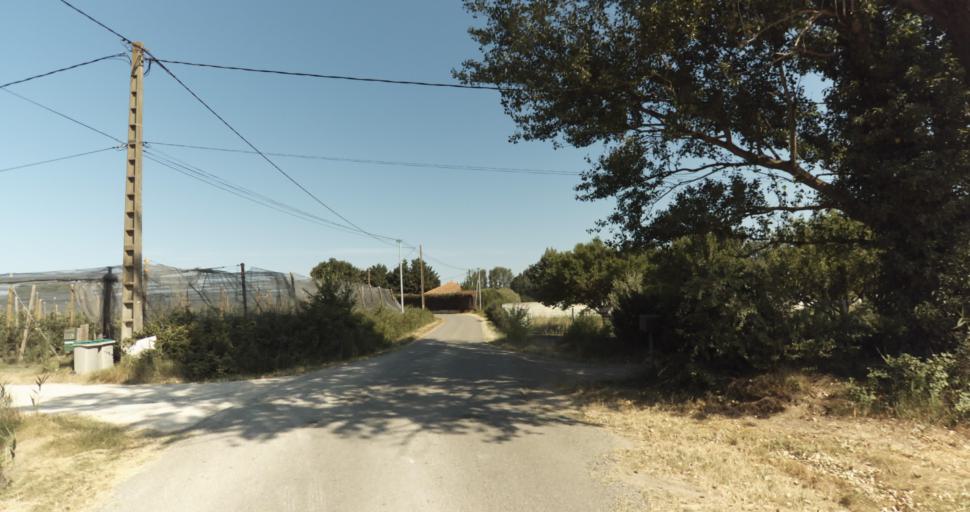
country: FR
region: Provence-Alpes-Cote d'Azur
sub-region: Departement du Vaucluse
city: Althen-des-Paluds
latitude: 44.0040
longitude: 4.9875
